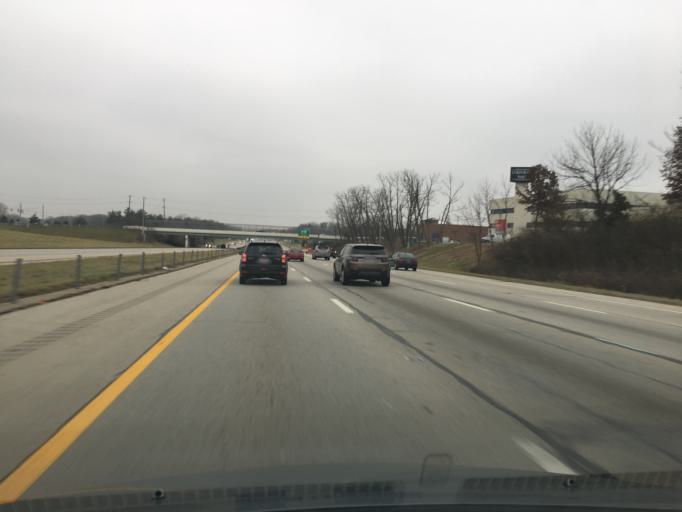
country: US
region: Ohio
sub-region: Hamilton County
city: Sixteen Mile Stand
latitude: 39.2631
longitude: -84.3407
